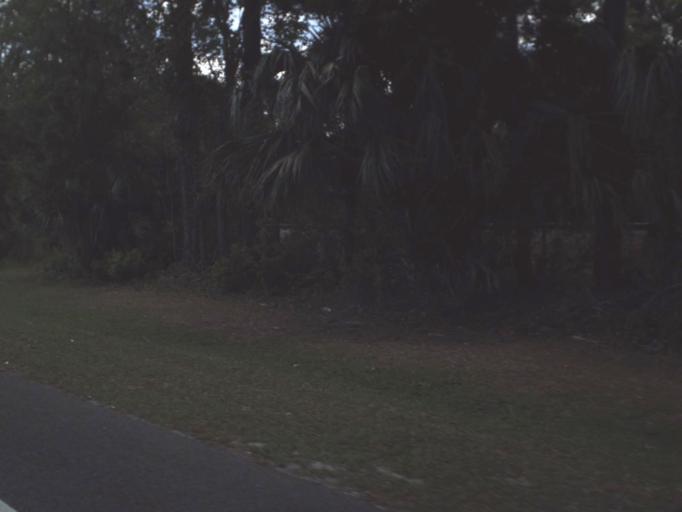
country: US
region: Florida
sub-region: Flagler County
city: Bunnell
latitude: 29.4573
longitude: -81.2504
